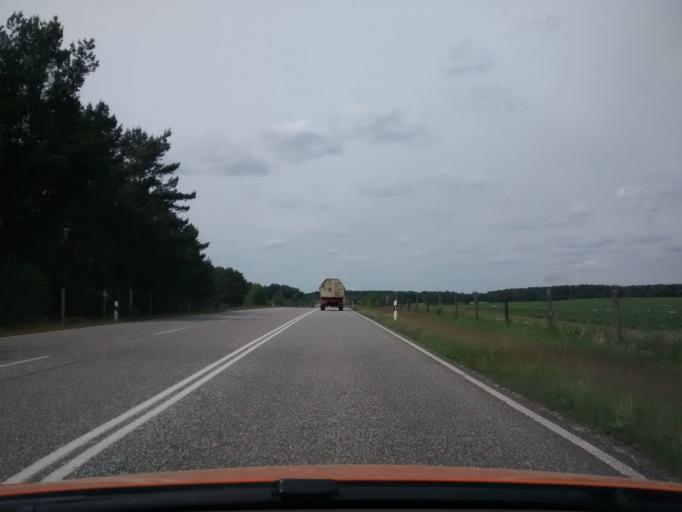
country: DE
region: Brandenburg
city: Luckenwalde
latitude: 52.1164
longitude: 13.1553
